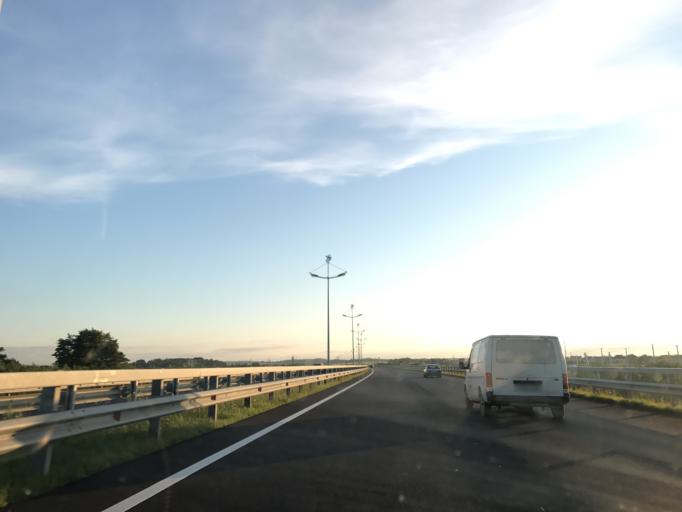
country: RU
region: Kaliningrad
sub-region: Zelenogradskiy Rayon
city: Zelenogradsk
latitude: 54.9236
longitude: 20.3832
